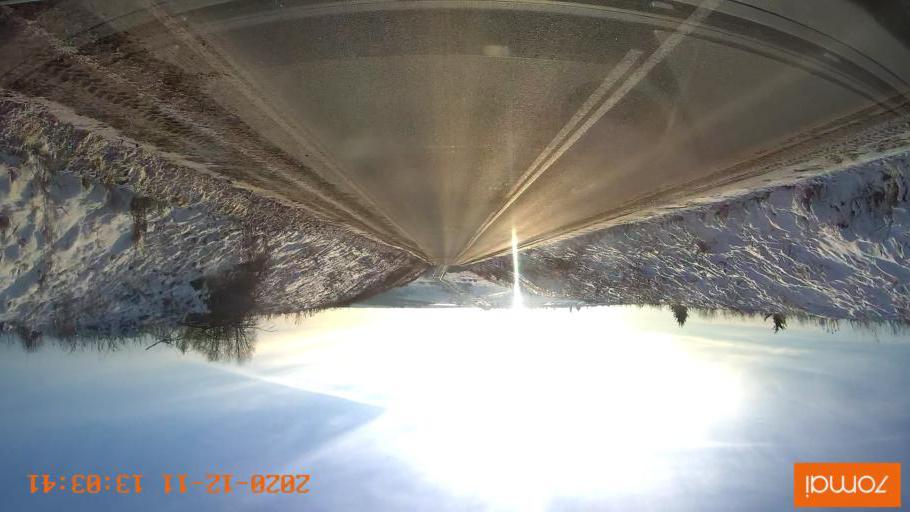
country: RU
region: Kostroma
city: Chistyye Bory
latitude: 58.2665
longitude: 41.6731
